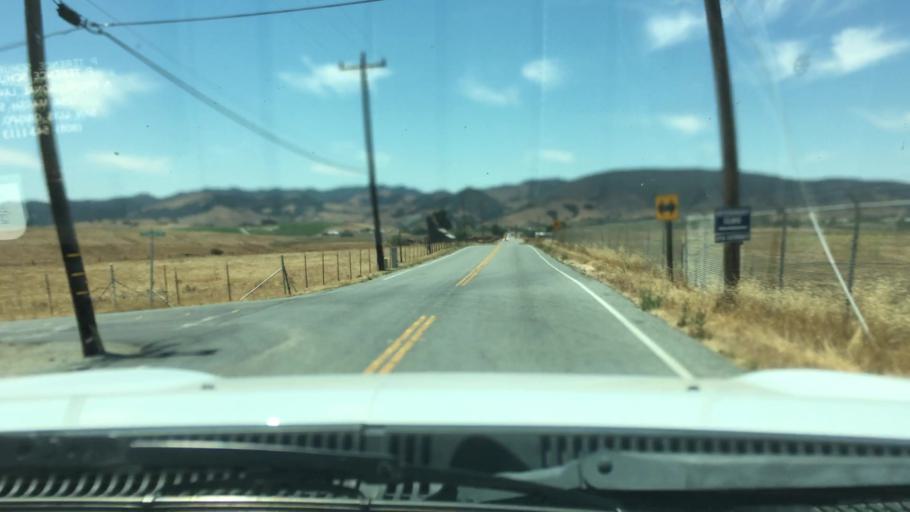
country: US
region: California
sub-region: San Luis Obispo County
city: San Luis Obispo
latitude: 35.2359
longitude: -120.6490
